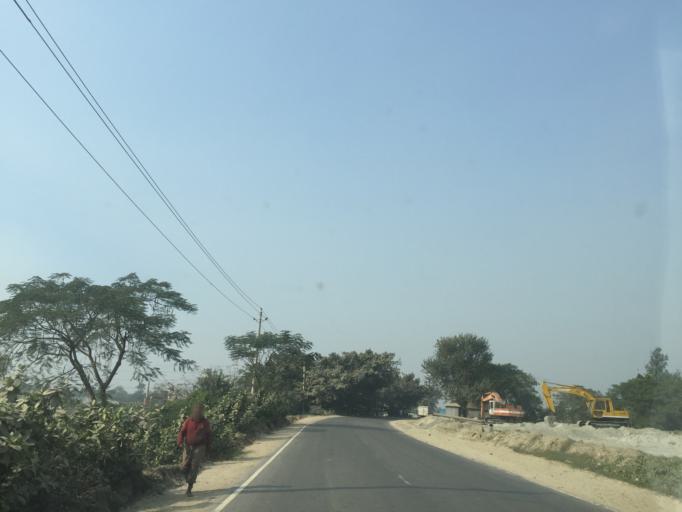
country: BD
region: Dhaka
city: Tungi
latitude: 23.8459
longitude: 90.3406
